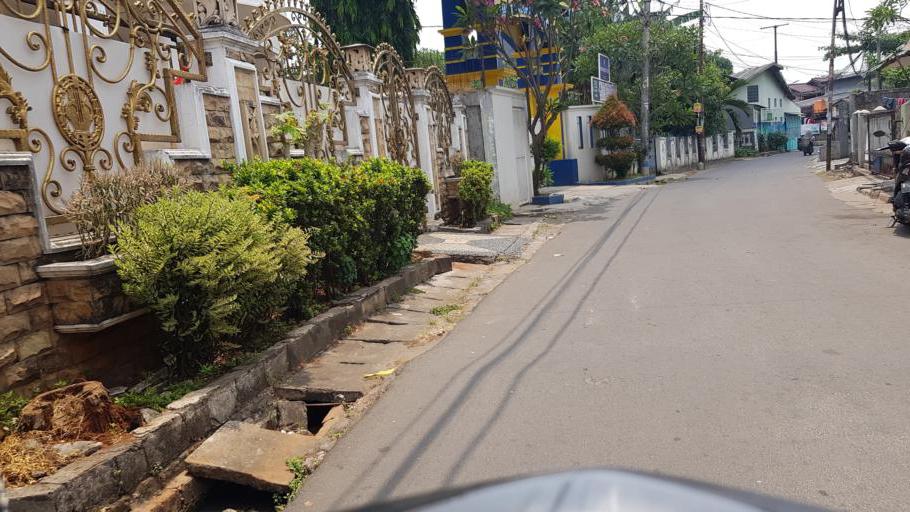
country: ID
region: West Java
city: Bekasi
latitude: -6.2801
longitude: 106.9309
